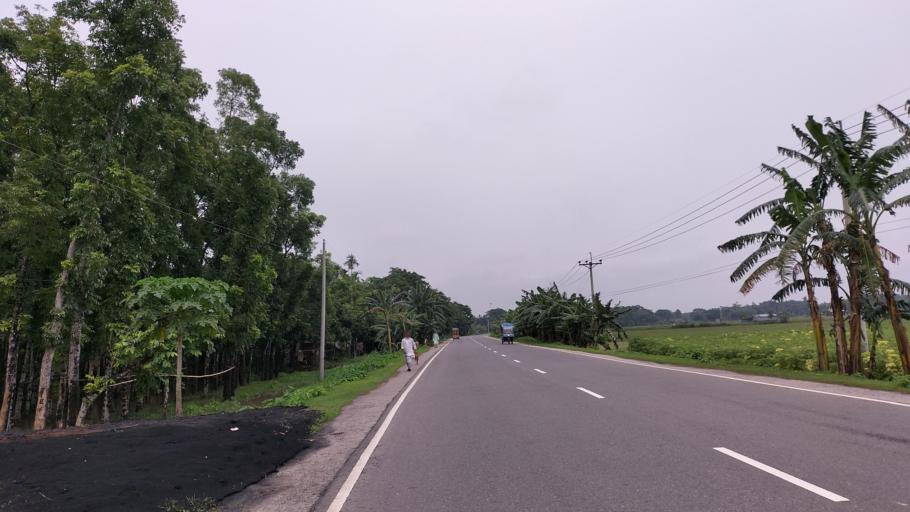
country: BD
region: Dhaka
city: Netrakona
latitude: 24.8524
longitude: 90.6174
